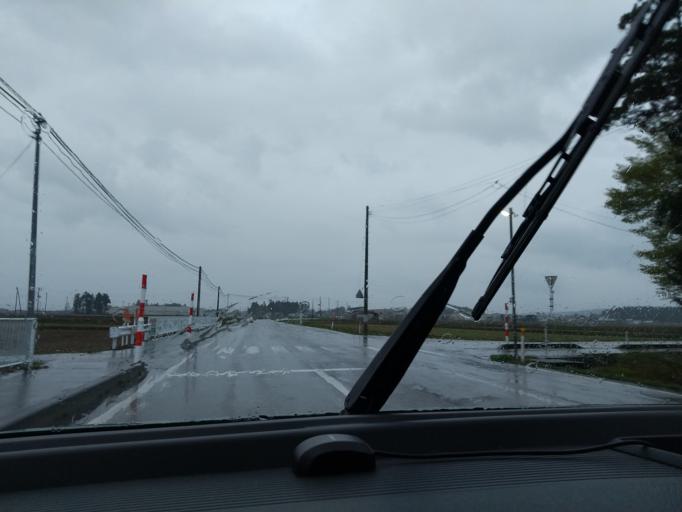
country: JP
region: Akita
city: Omagari
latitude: 39.4115
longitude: 140.5401
